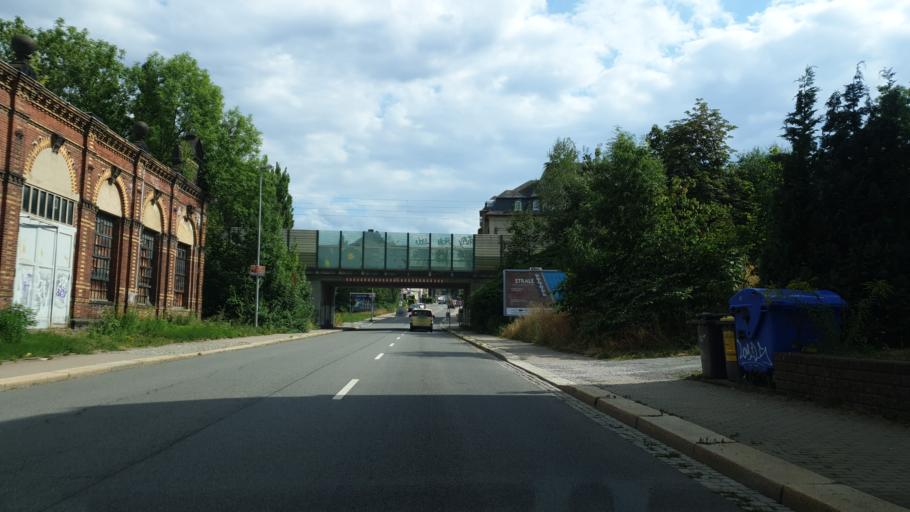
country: DE
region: Saxony
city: Chemnitz
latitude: 50.8220
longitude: 12.8947
